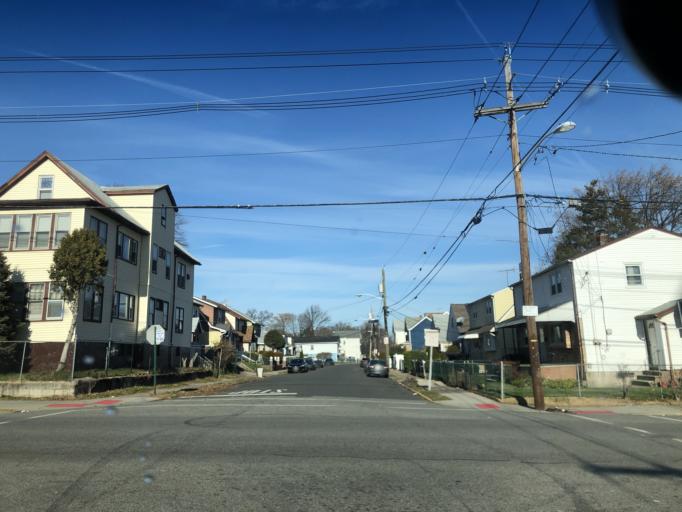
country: US
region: New Jersey
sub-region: Bergen County
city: Fair Lawn
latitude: 40.9234
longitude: -74.1445
